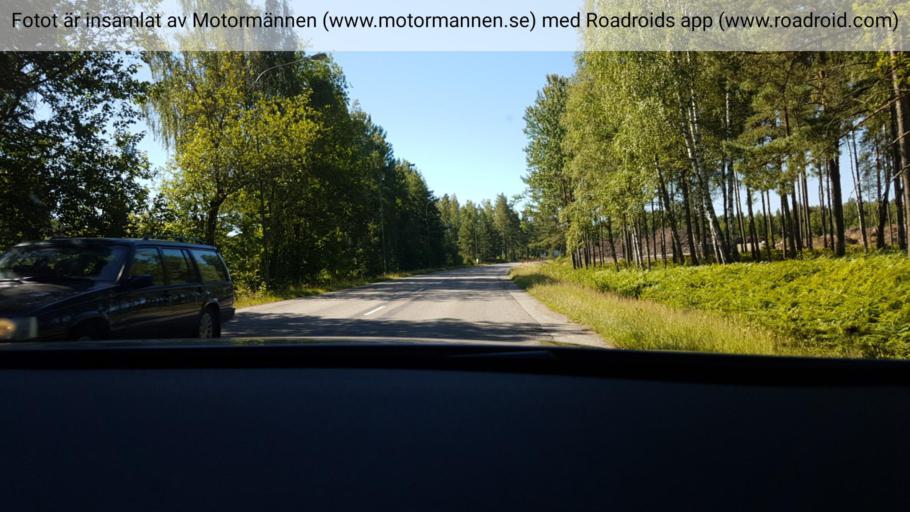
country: SE
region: Vaestra Goetaland
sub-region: Tidaholms Kommun
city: Tidaholm
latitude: 58.1671
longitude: 13.9632
